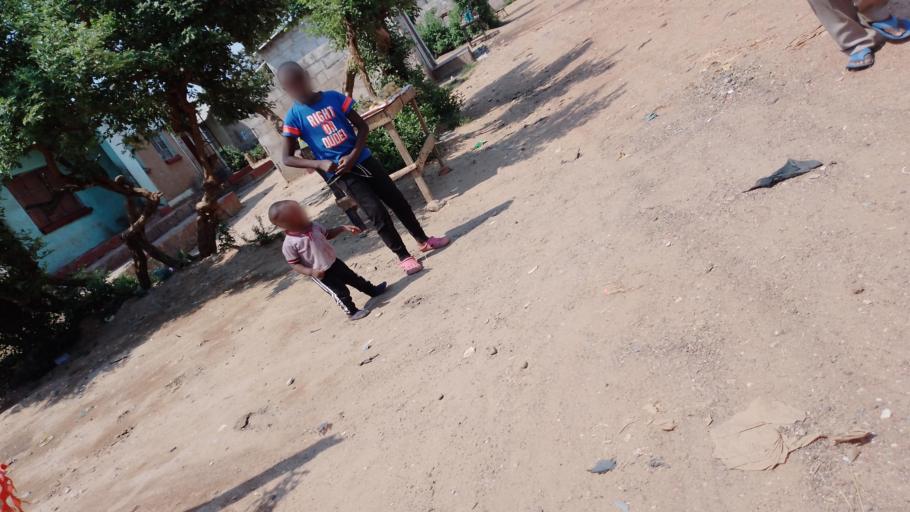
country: ZM
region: Lusaka
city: Lusaka
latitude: -15.3990
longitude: 28.3661
